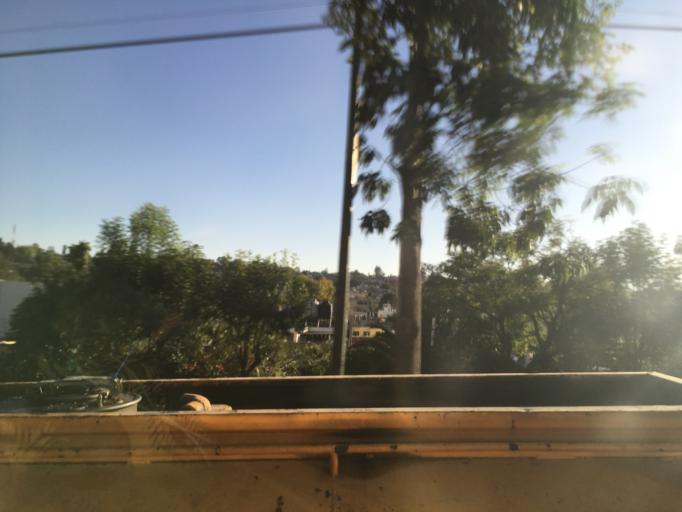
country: MX
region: Mexico City
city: Polanco
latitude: 19.3967
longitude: -99.2085
